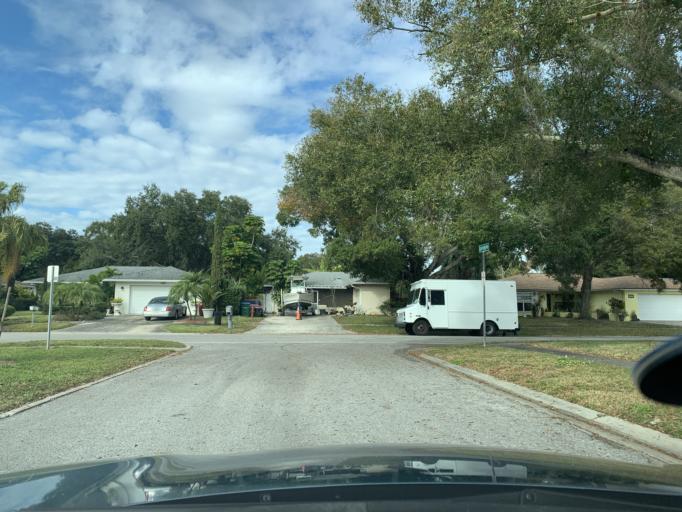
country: US
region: Florida
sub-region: Pinellas County
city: Kenneth City
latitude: 27.8244
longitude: -82.7346
